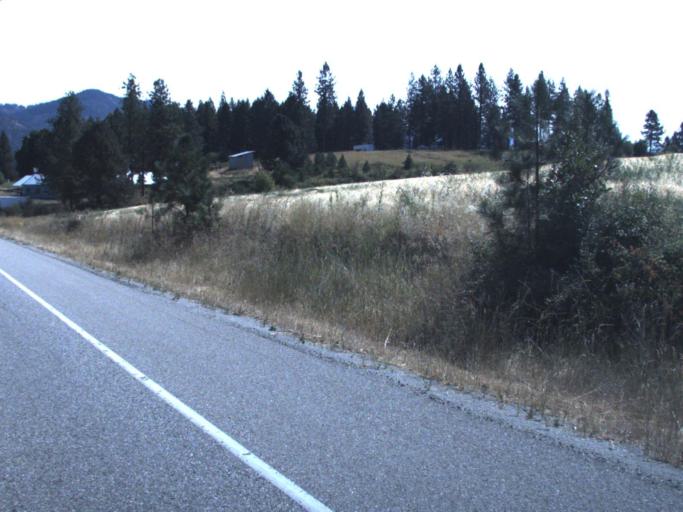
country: US
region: Washington
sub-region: Stevens County
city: Chewelah
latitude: 48.2915
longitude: -117.7359
